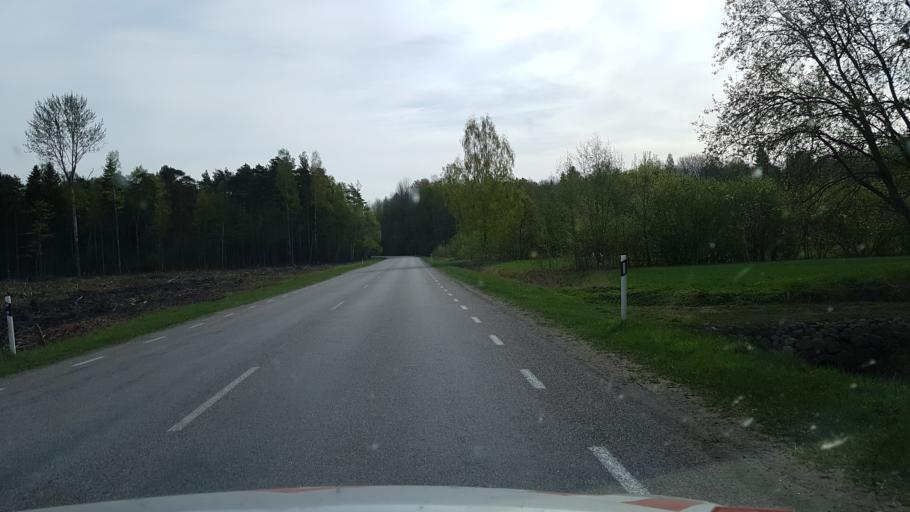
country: EE
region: Paernumaa
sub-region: Audru vald
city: Audru
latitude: 58.4066
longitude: 24.3136
